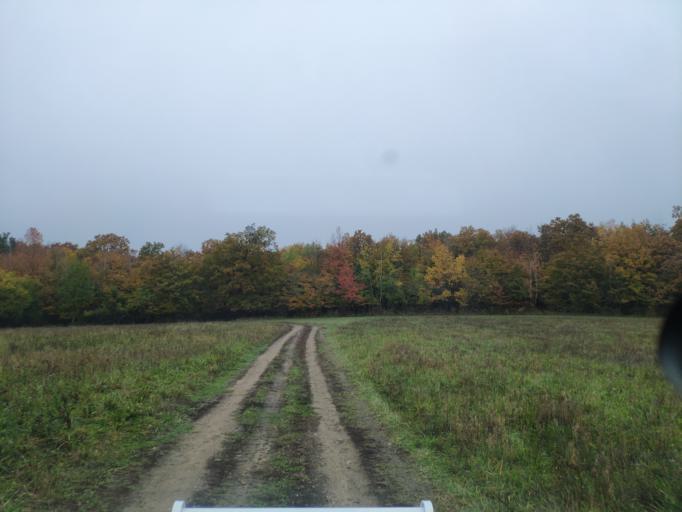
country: SK
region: Kosicky
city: Moldava nad Bodvou
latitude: 48.7144
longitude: 21.0127
